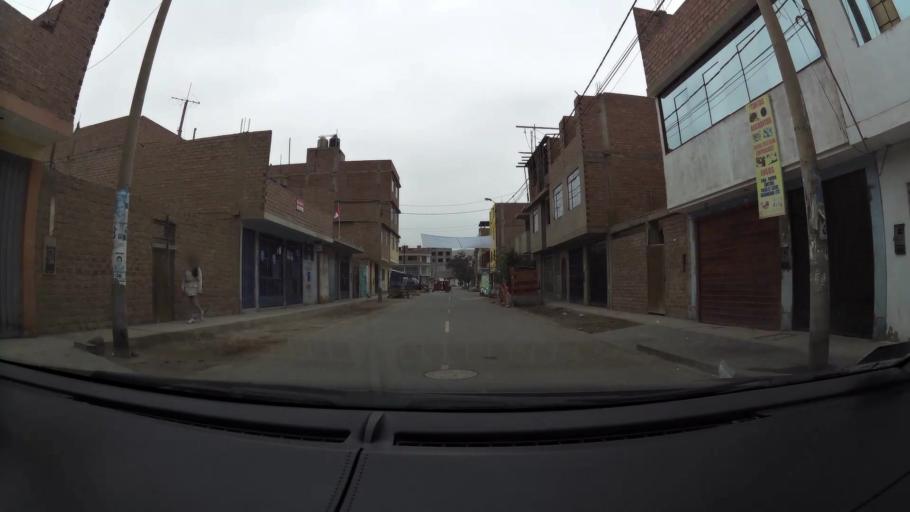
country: PE
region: Lima
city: Ventanilla
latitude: -11.9352
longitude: -77.0898
